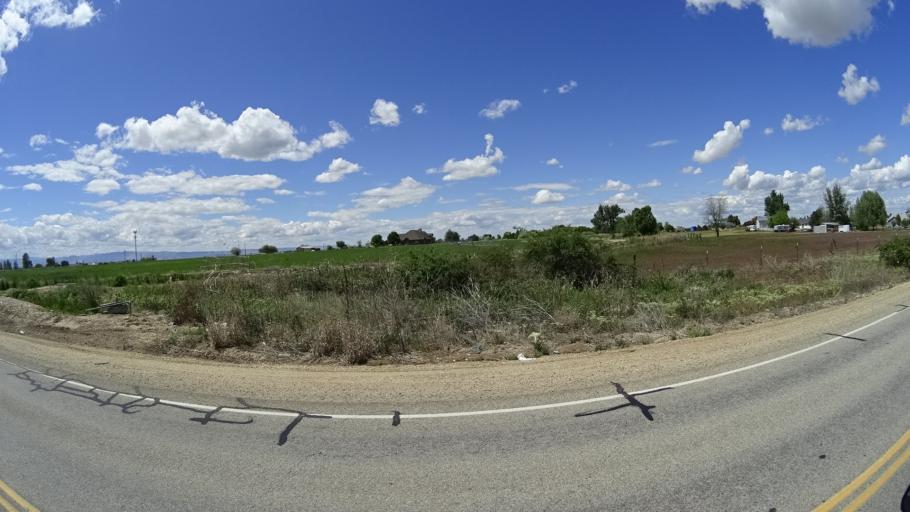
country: US
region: Idaho
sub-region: Ada County
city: Meridian
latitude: 43.5650
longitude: -116.4337
